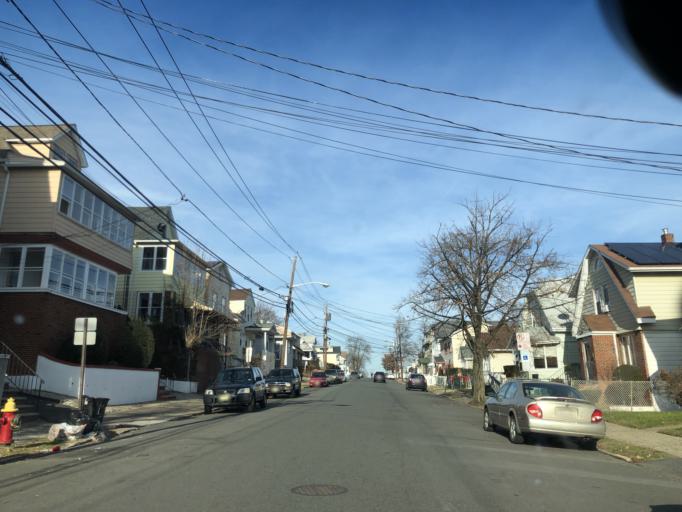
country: US
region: New Jersey
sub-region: Bergen County
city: Fair Lawn
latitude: 40.9302
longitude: -74.1454
